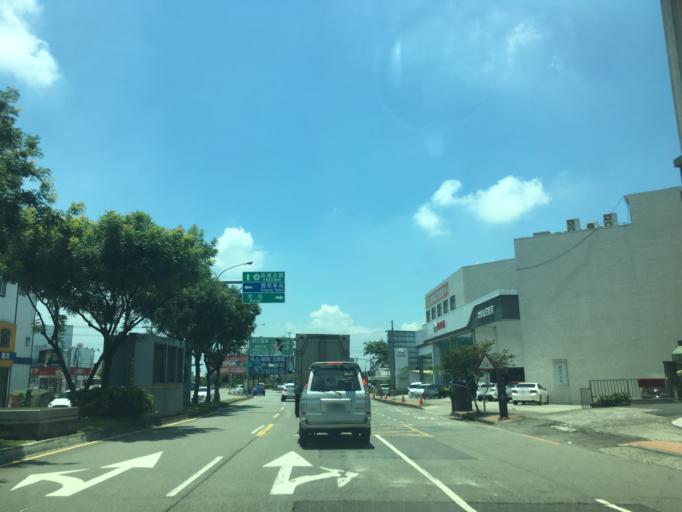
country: TW
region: Taiwan
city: Fengyuan
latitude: 24.2395
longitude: 120.7031
